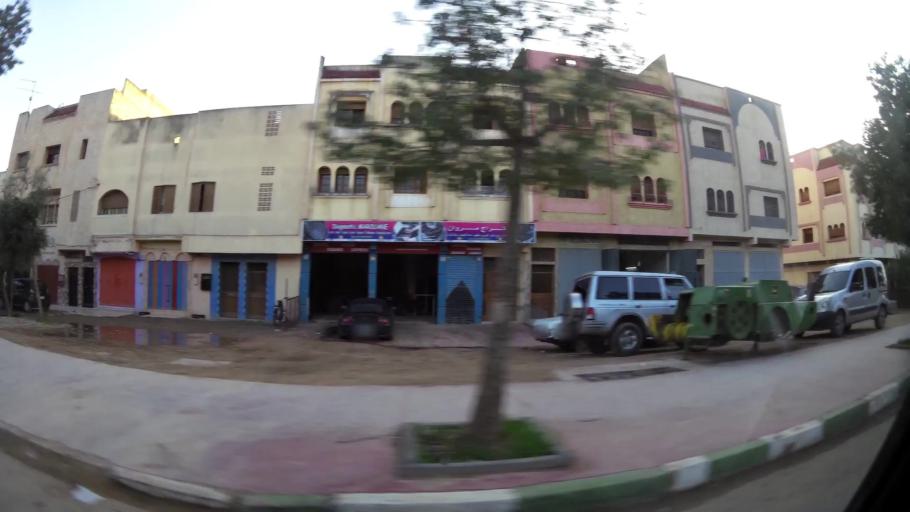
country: MA
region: Chaouia-Ouardigha
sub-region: Settat Province
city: Settat
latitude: 32.9912
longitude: -7.6122
